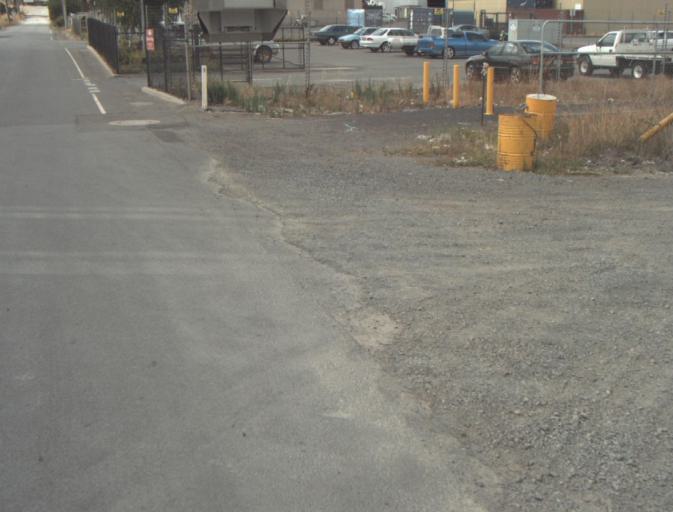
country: AU
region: Tasmania
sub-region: Launceston
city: Newnham
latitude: -41.4047
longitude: 147.1479
